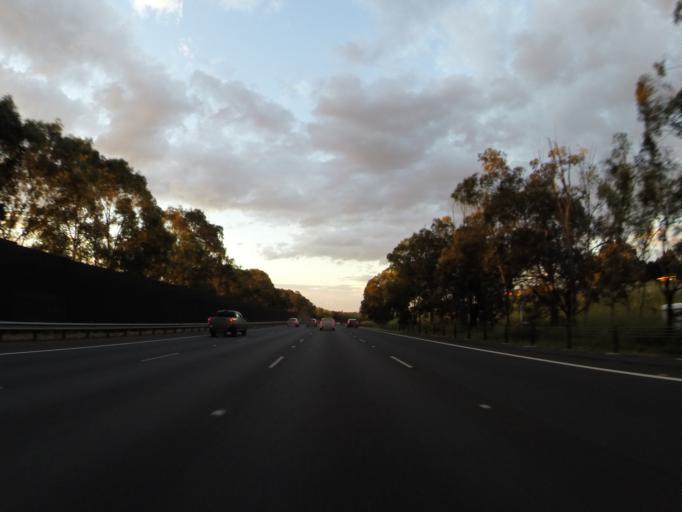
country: AU
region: New South Wales
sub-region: Campbelltown Municipality
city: Leumeah
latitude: -34.0212
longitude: 150.8242
